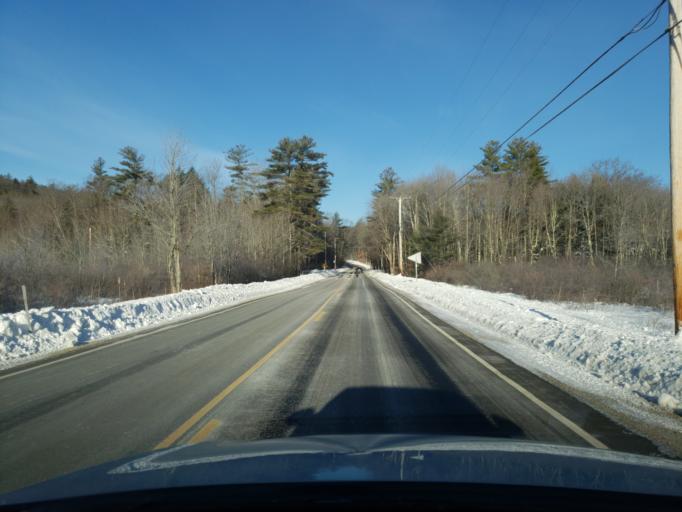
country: US
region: New Hampshire
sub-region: Hillsborough County
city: Greenfield
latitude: 42.9971
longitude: -71.8247
